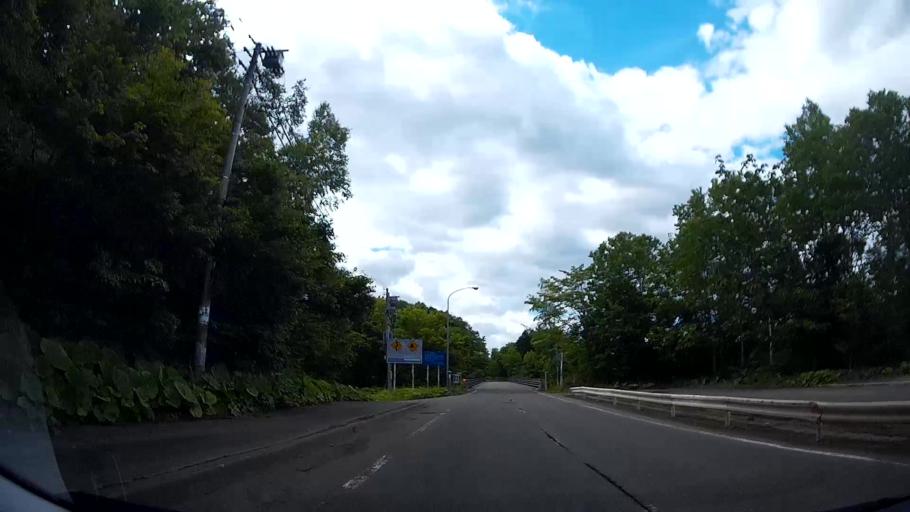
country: JP
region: Hokkaido
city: Kitahiroshima
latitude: 42.8440
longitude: 141.4394
